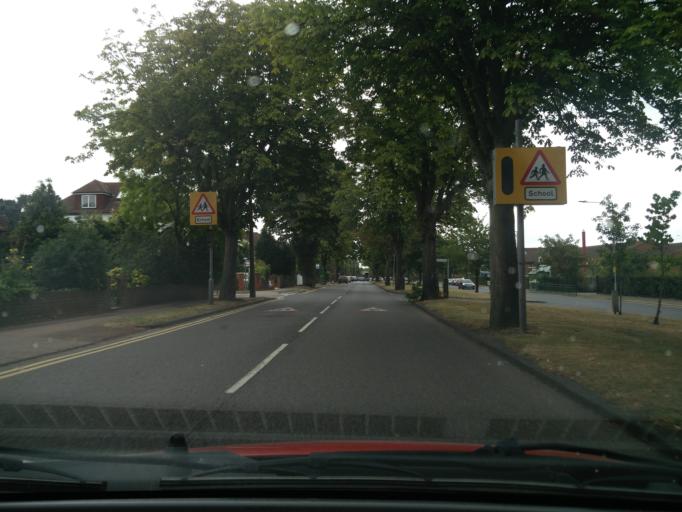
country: GB
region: England
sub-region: Southend-on-Sea
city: Westcliff-on-Sea
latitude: 51.5535
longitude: 0.6821
